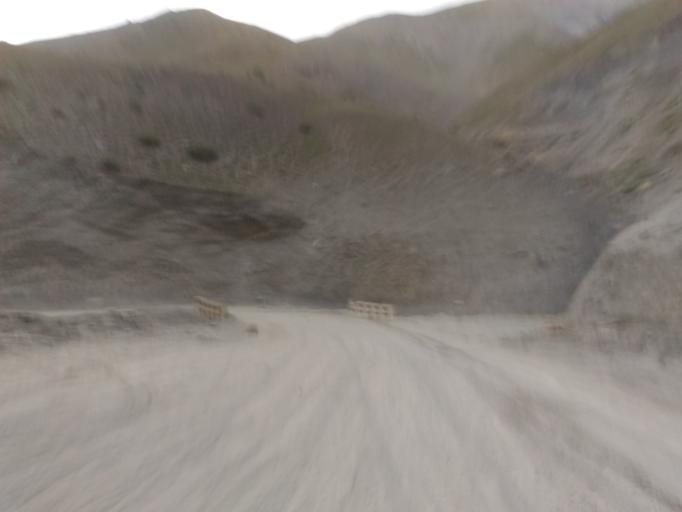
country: IN
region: Himachal Pradesh
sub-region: Lahul and Spiti
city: Kyelang
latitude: 32.5156
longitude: 76.9817
